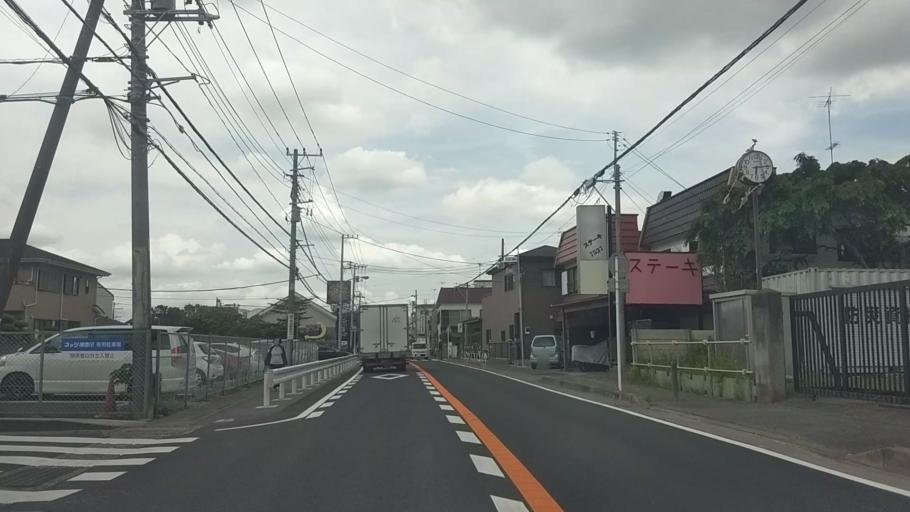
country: JP
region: Kanagawa
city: Fujisawa
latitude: 35.3278
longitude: 139.5093
